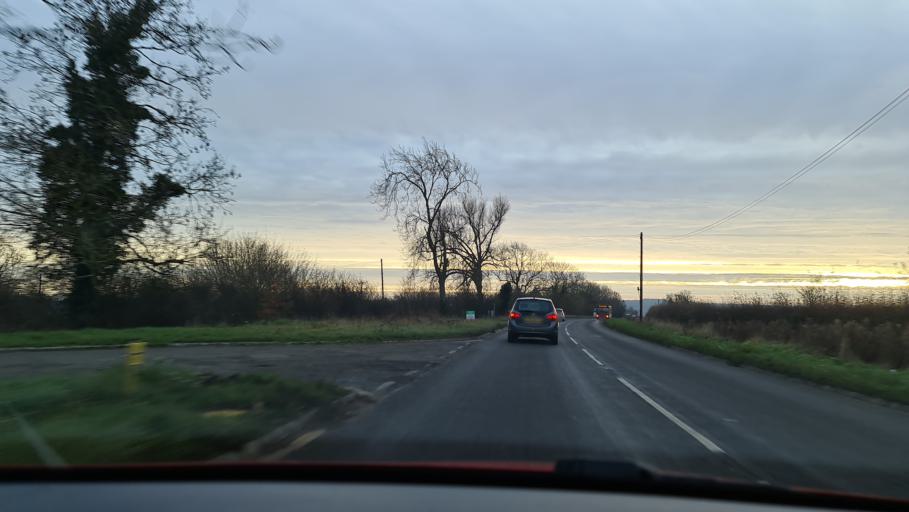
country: GB
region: England
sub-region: Buckinghamshire
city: Haddenham
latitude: 51.7507
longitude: -0.8801
